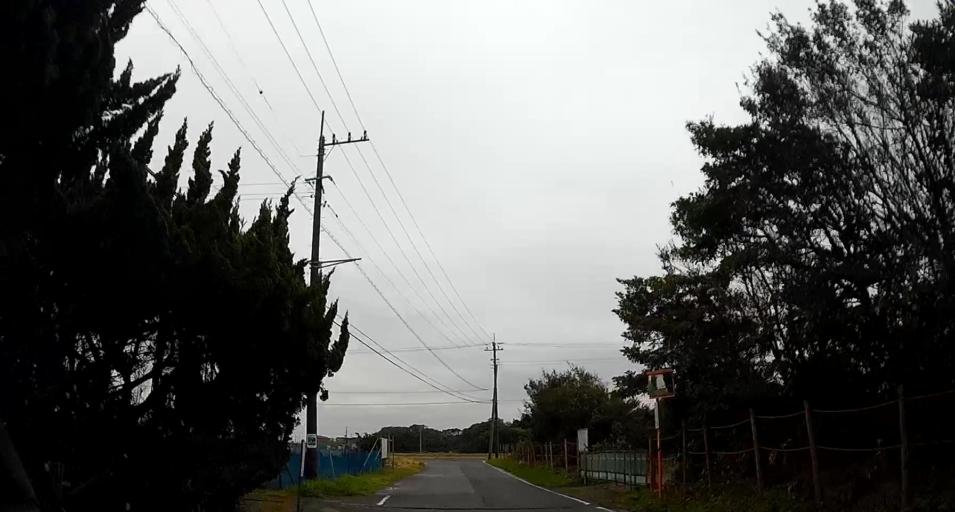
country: JP
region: Chiba
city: Kisarazu
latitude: 35.4211
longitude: 139.9013
